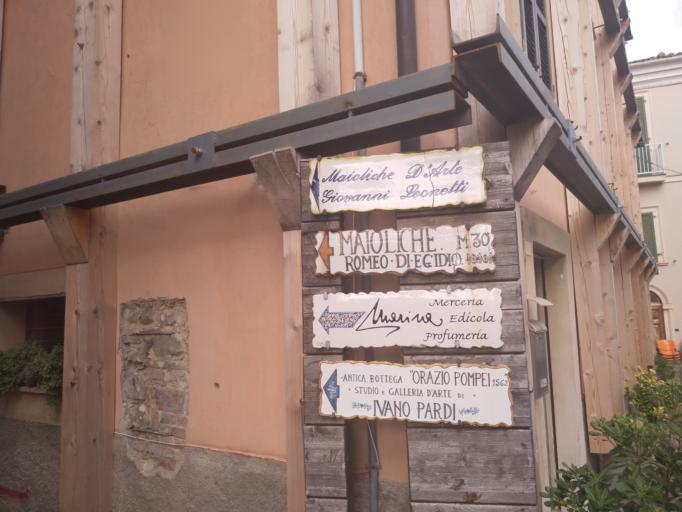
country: IT
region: Abruzzo
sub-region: Provincia di Teramo
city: Castelli
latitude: 42.4894
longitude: 13.7118
